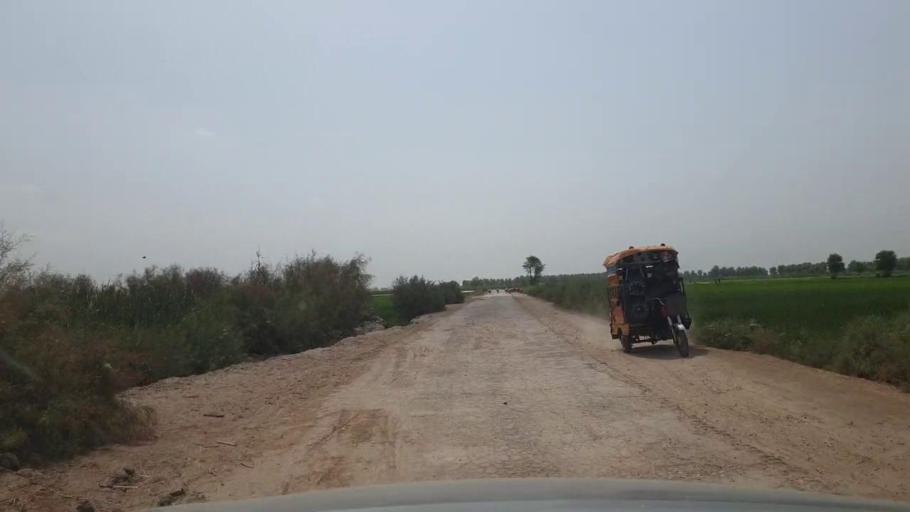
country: PK
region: Sindh
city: Garhi Yasin
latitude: 27.9420
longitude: 68.3798
